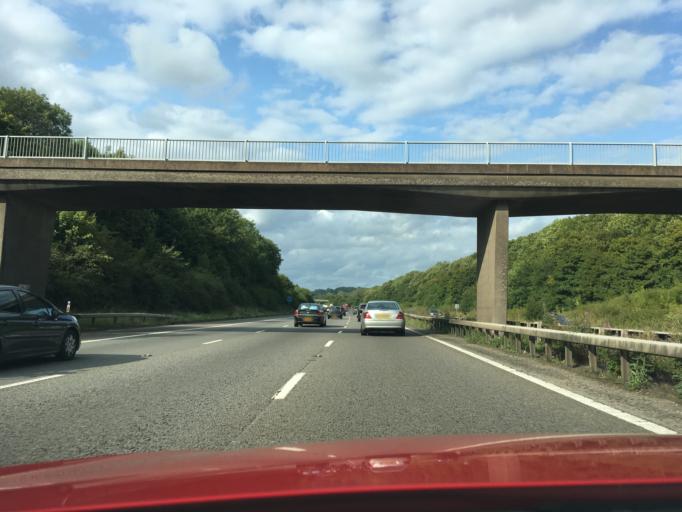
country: GB
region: England
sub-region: South Gloucestershire
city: Charfield
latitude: 51.6688
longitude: -2.4095
